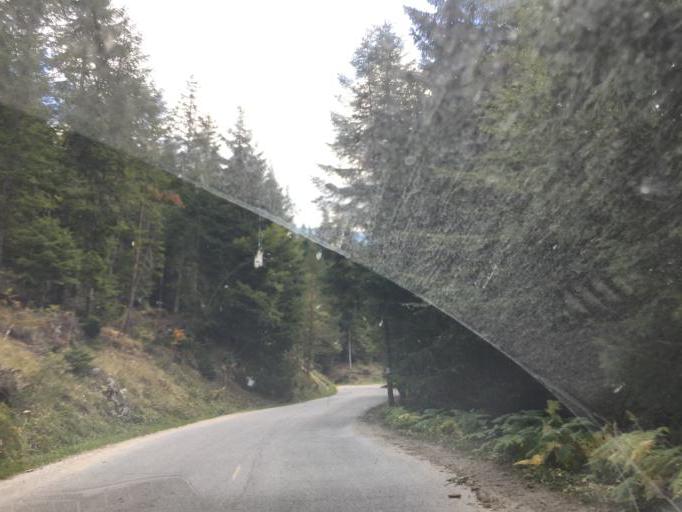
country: BG
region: Pazardzhik
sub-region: Obshtina Batak
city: Batak
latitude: 41.9129
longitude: 24.2855
